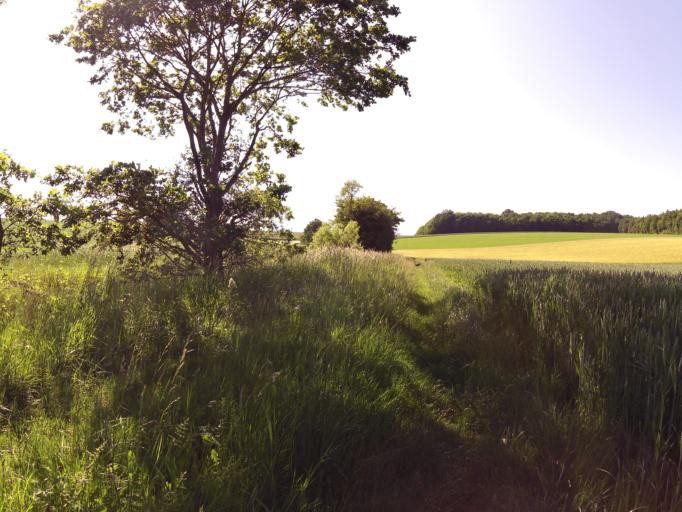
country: DE
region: Bavaria
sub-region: Regierungsbezirk Unterfranken
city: Kleinrinderfeld
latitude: 49.7130
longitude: 9.8578
